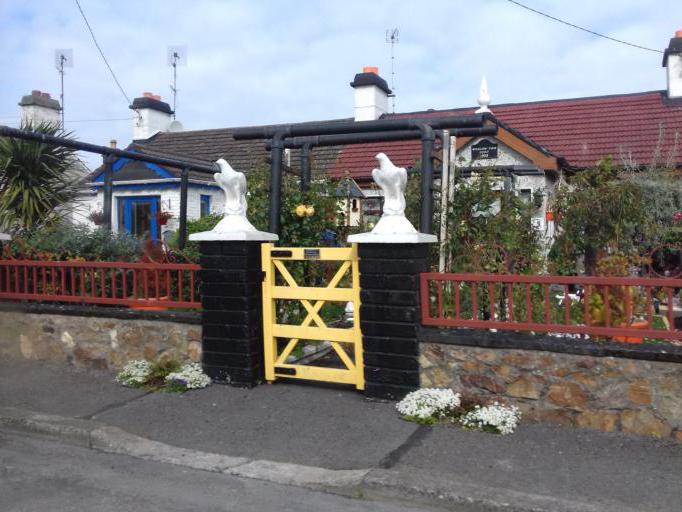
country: IE
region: Leinster
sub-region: Dublin City
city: Finglas
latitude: 53.4078
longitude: -6.2988
